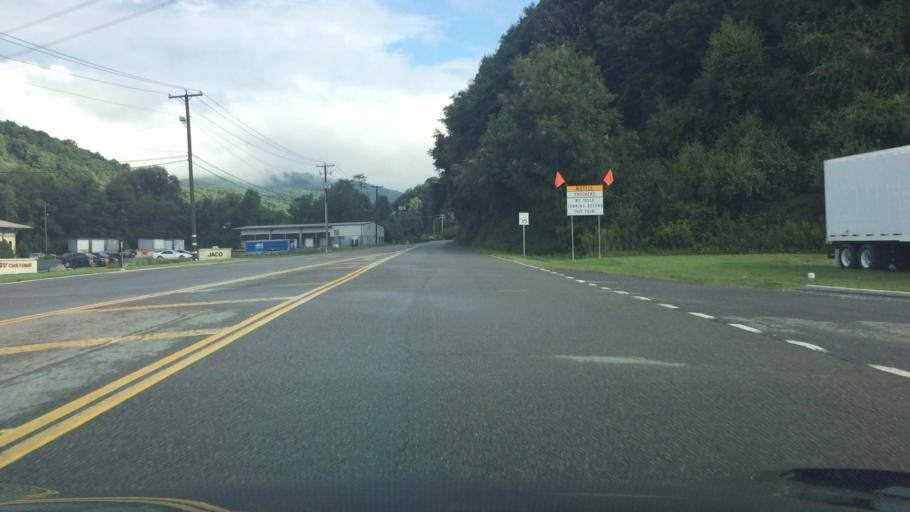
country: US
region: Virginia
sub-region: Smyth County
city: Atkins
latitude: 36.8605
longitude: -81.4327
